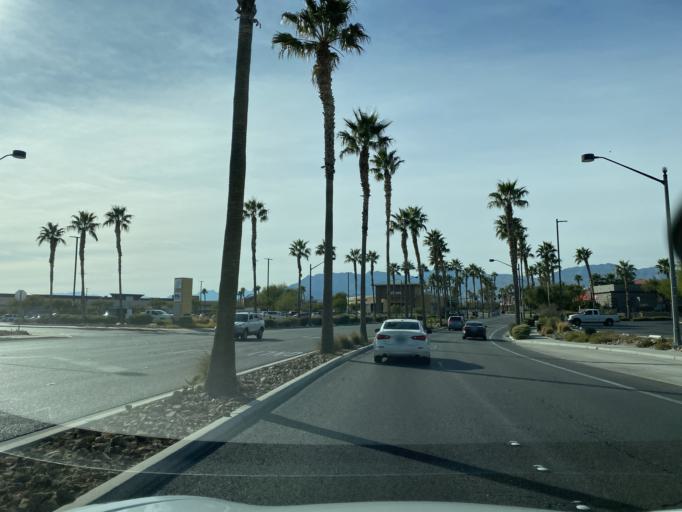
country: US
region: Nevada
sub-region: Clark County
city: Las Vegas
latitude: 36.2715
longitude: -115.2650
